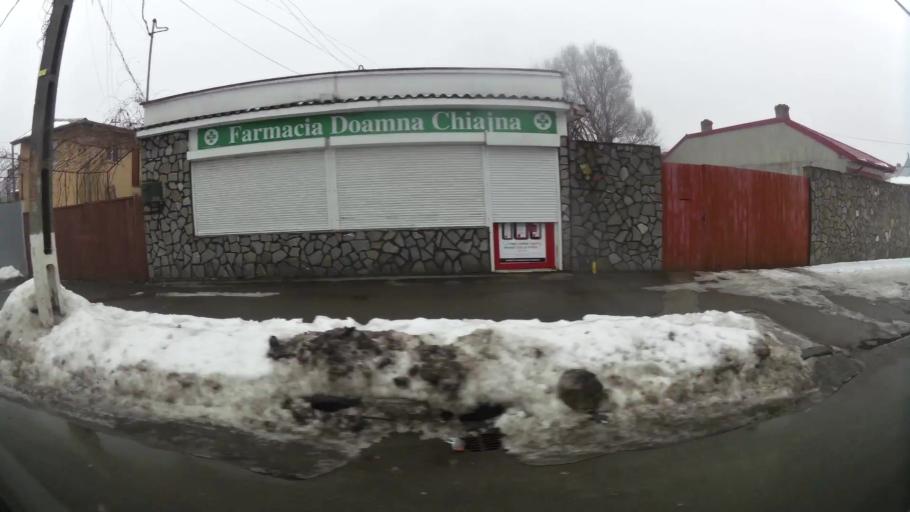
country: RO
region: Ilfov
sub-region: Comuna Chiajna
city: Chiajna
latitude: 44.4609
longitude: 25.9752
